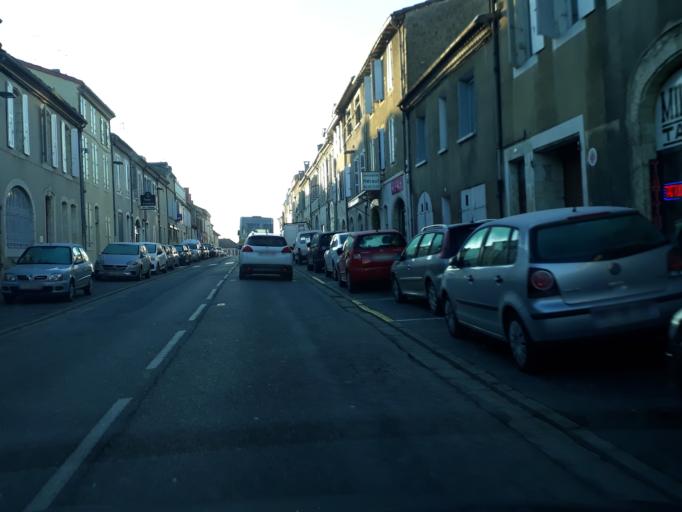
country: FR
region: Midi-Pyrenees
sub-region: Departement du Gers
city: Auch
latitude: 43.6433
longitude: 0.5837
